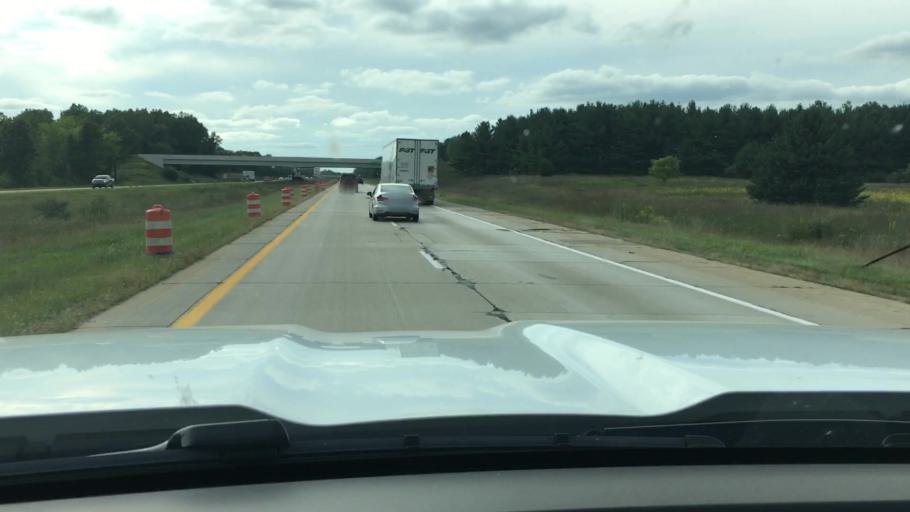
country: US
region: Michigan
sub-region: Lapeer County
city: Imlay City
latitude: 43.0085
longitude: -83.1610
